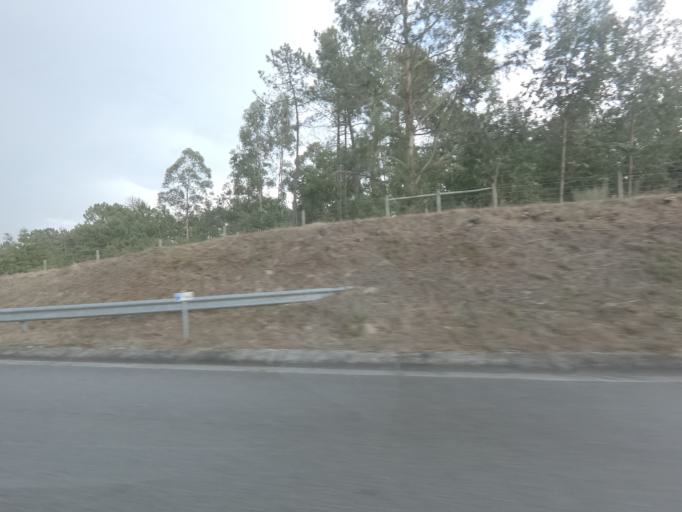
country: PT
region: Viseu
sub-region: Viseu
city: Abraveses
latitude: 40.6976
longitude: -7.9583
